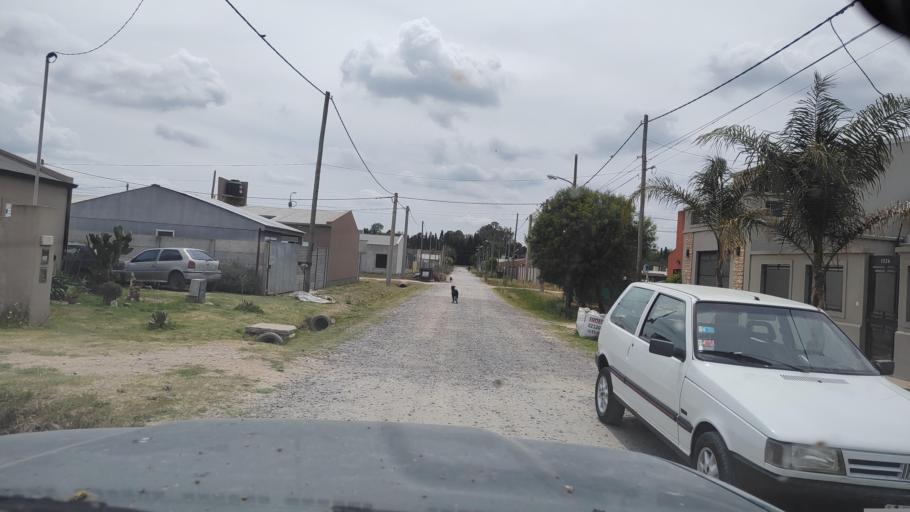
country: AR
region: Buenos Aires
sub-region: Partido de Lujan
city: Lujan
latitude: -34.5546
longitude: -59.1368
